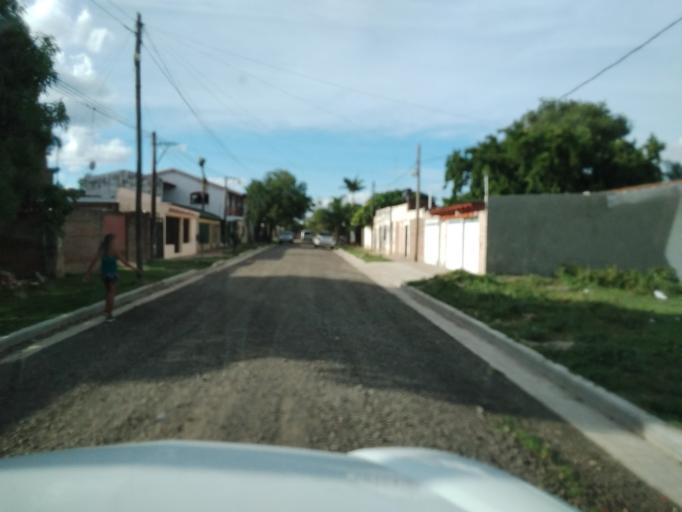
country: AR
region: Corrientes
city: Corrientes
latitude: -27.4919
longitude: -58.8431
